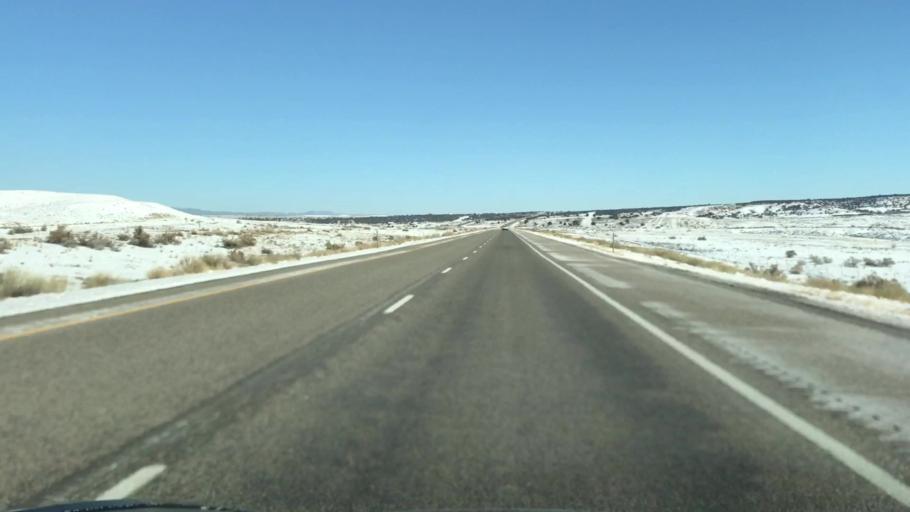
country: US
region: Colorado
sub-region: Mesa County
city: Loma
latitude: 39.1482
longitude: -109.1491
